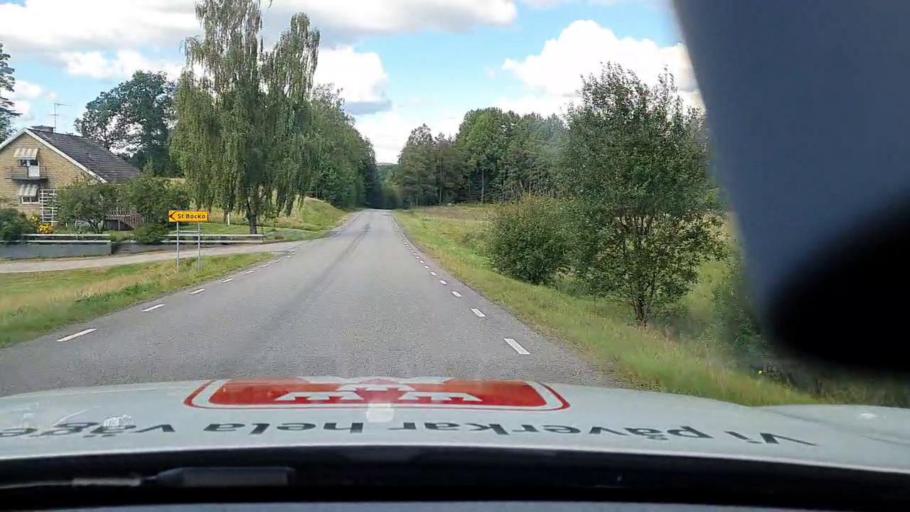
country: SE
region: Vaestra Goetaland
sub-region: Marks Kommun
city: Fritsla
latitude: 57.3977
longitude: 12.8509
